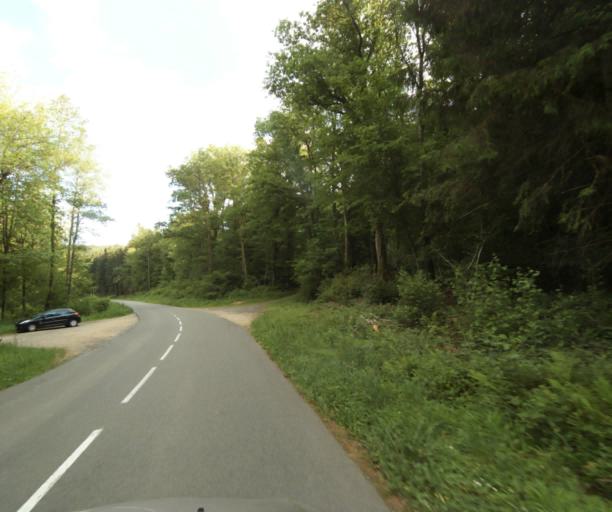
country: FR
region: Champagne-Ardenne
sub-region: Departement des Ardennes
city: Nouzonville
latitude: 49.8232
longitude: 4.7127
